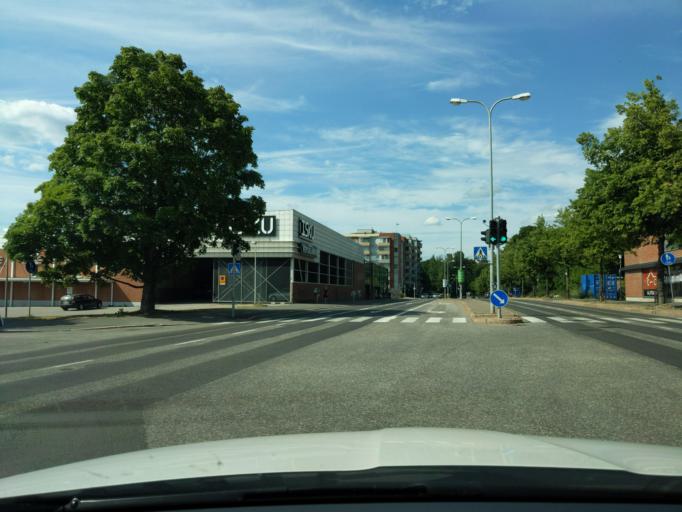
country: FI
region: Paijanne Tavastia
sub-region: Lahti
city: Lahti
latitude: 60.9885
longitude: 25.6673
